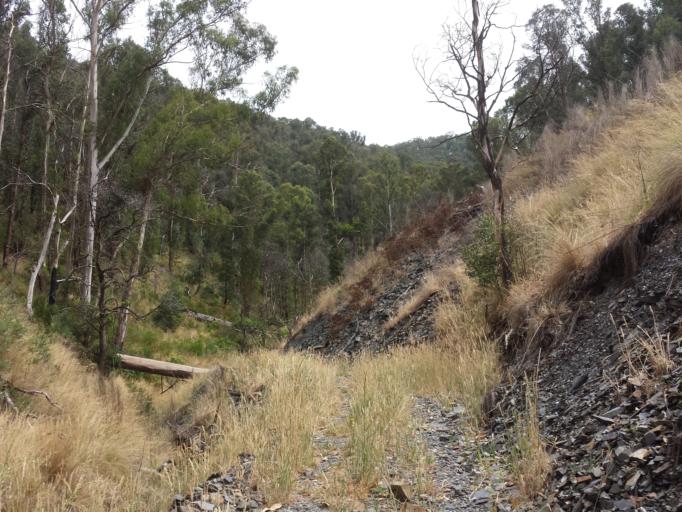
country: AU
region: Victoria
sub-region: Wellington
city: Heyfield
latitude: -37.7344
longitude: 146.4042
